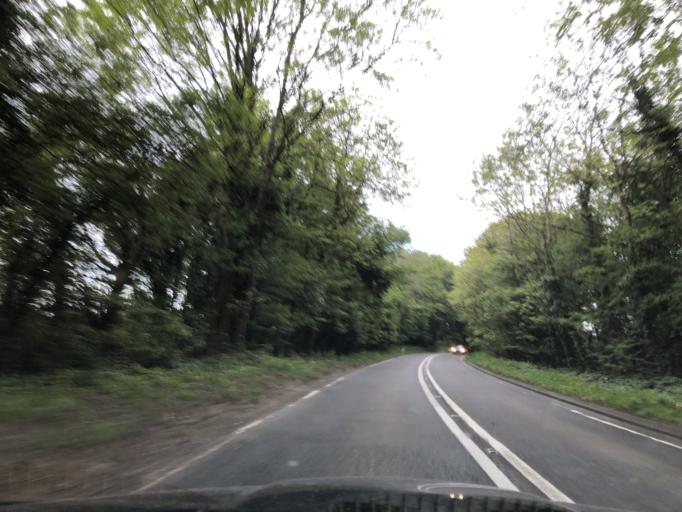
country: GB
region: England
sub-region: Gloucestershire
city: Donnington
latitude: 51.9471
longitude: -1.7178
